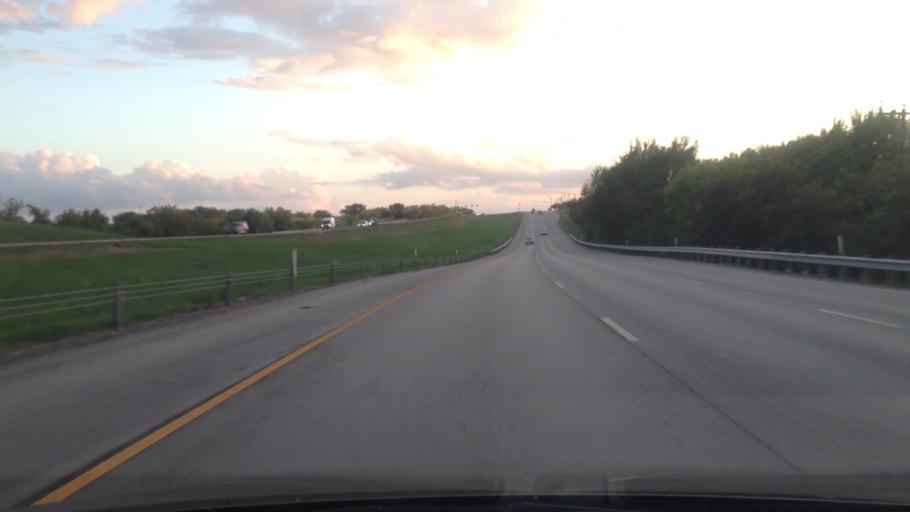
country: US
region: Texas
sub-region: Tarrant County
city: Benbrook
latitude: 32.6545
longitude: -97.4961
